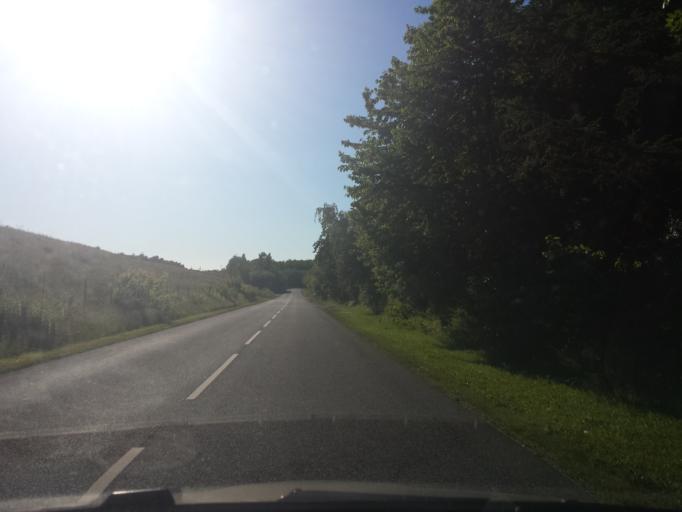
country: DK
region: Capital Region
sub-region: Glostrup Kommune
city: Glostrup
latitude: 55.6987
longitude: 12.3844
